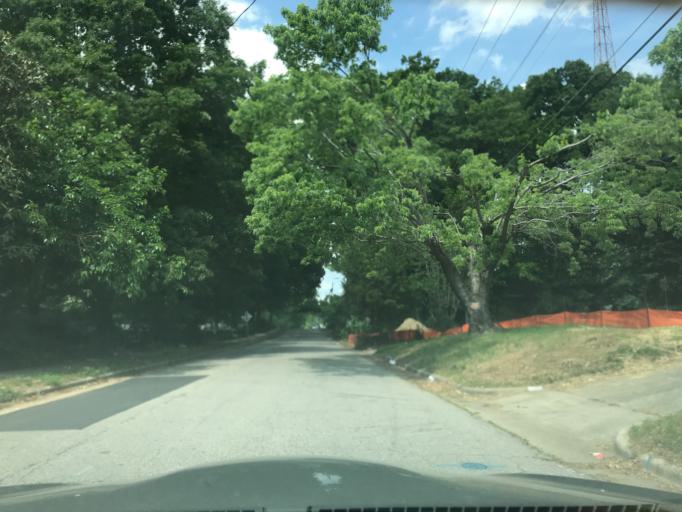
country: US
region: North Carolina
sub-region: Wake County
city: Raleigh
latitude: 35.7726
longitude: -78.6197
